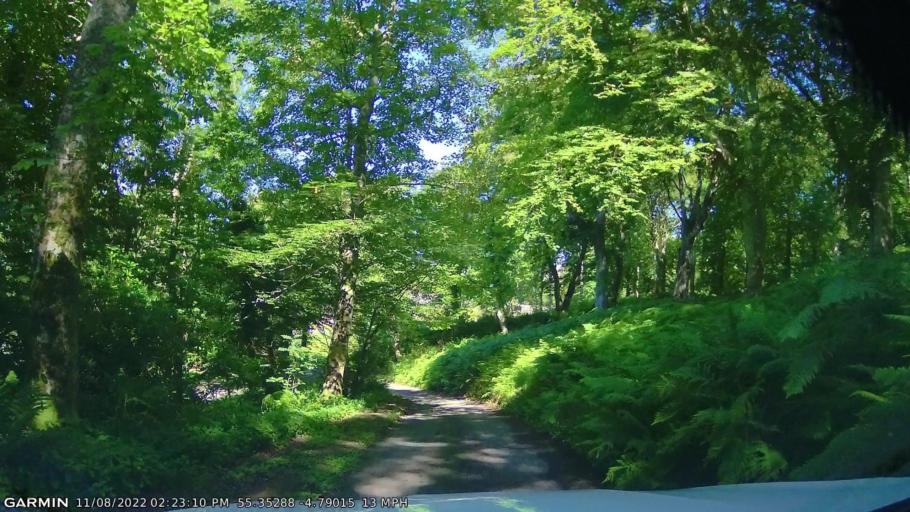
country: GB
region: Scotland
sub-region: South Ayrshire
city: Maybole
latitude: 55.3529
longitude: -4.7902
